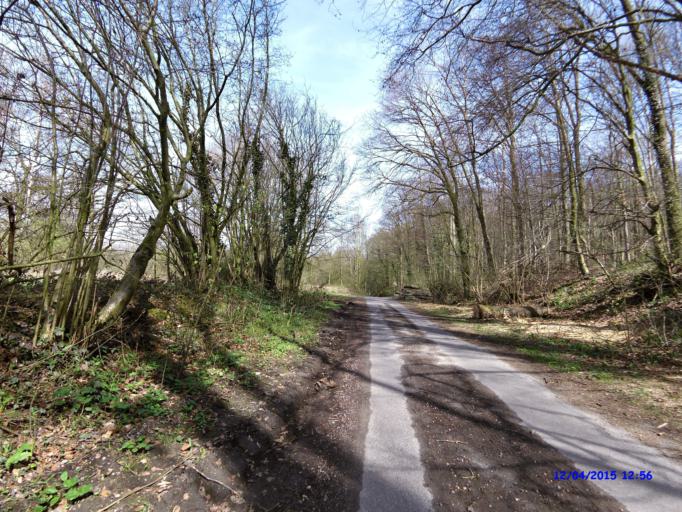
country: DE
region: North Rhine-Westphalia
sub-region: Regierungsbezirk Koln
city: Ubach-Palenberg
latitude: 50.9087
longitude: 6.0873
